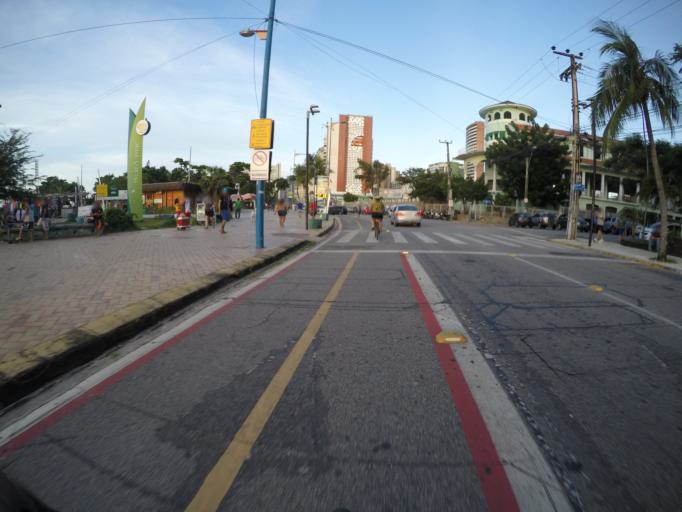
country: BR
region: Ceara
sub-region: Fortaleza
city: Fortaleza
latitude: -3.7260
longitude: -38.4954
